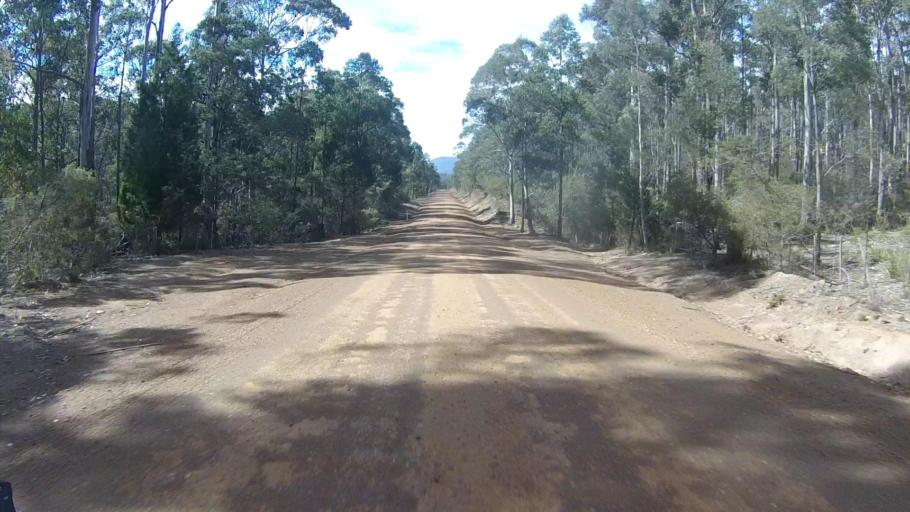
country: AU
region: Tasmania
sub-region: Sorell
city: Sorell
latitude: -42.6154
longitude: 147.8995
